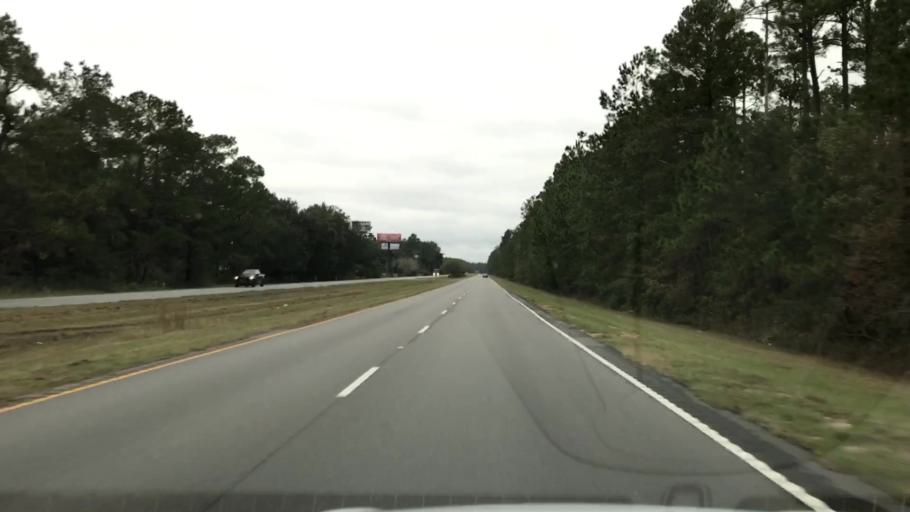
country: US
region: South Carolina
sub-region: Georgetown County
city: Georgetown
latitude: 33.2327
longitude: -79.3760
